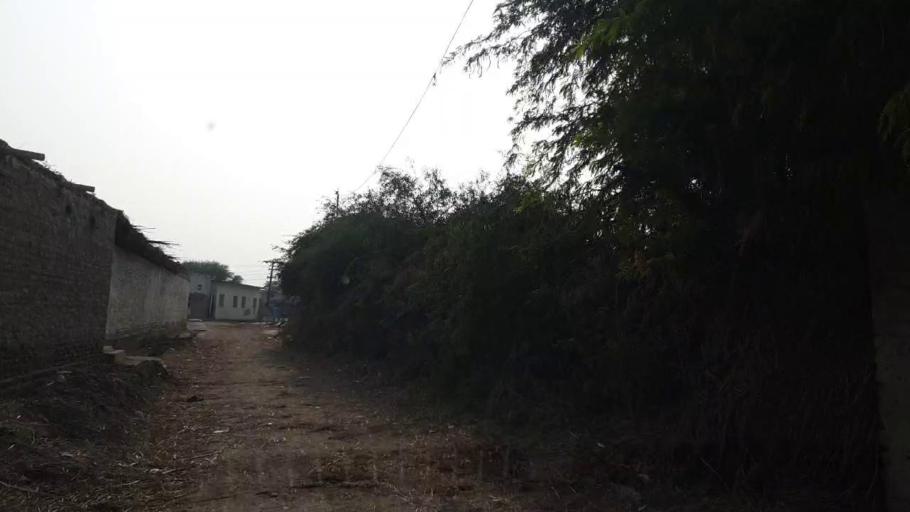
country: PK
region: Sindh
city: Tando Muhammad Khan
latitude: 25.1027
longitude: 68.5814
